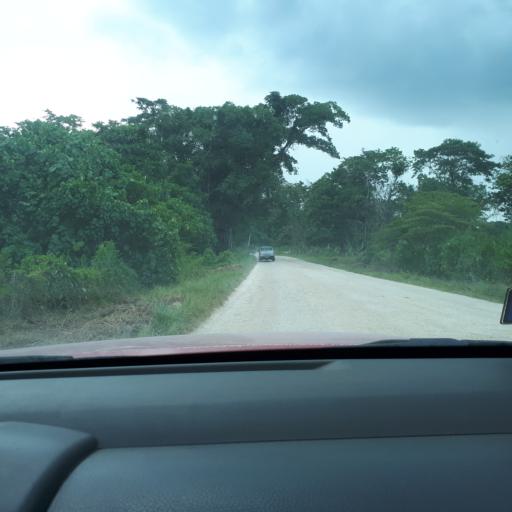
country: VU
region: Sanma
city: Luganville
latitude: -15.5787
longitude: 167.0287
